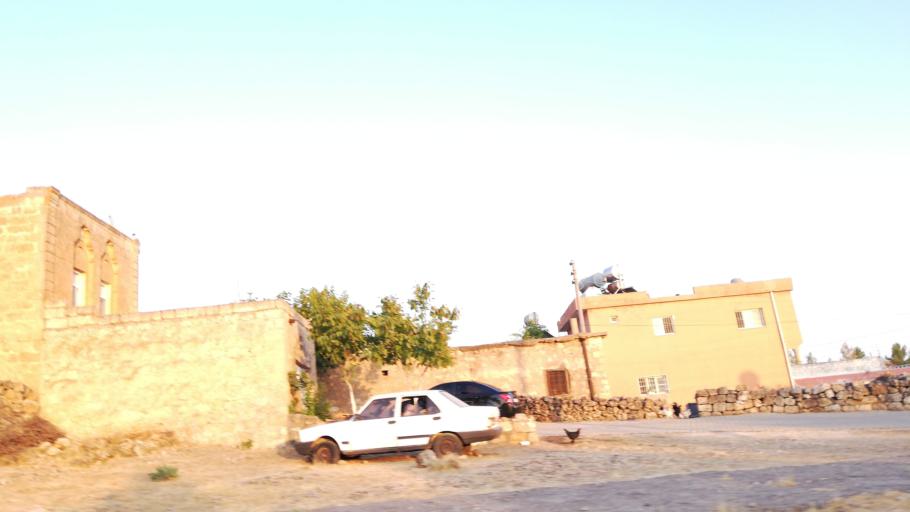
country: TR
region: Mardin
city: Kindirip
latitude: 37.4489
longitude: 41.2168
